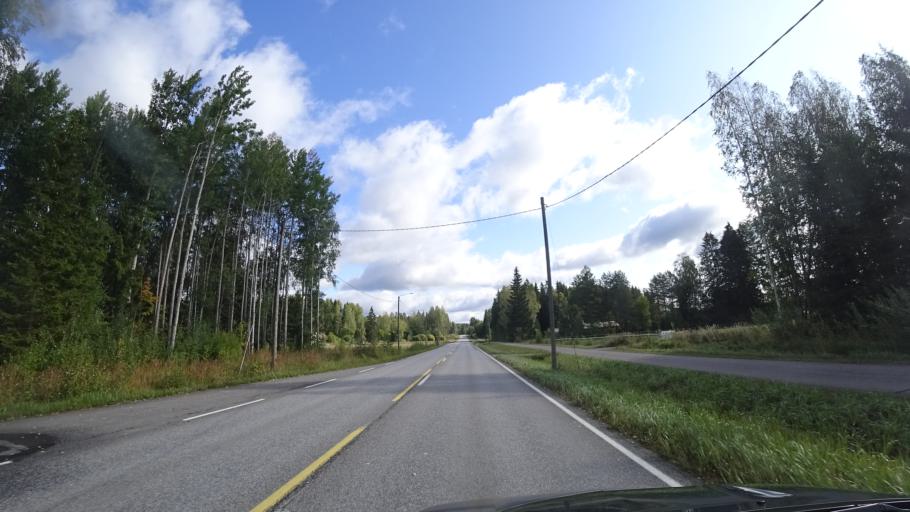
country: FI
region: Uusimaa
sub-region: Helsinki
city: Hyvinge
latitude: 60.5781
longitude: 24.9911
